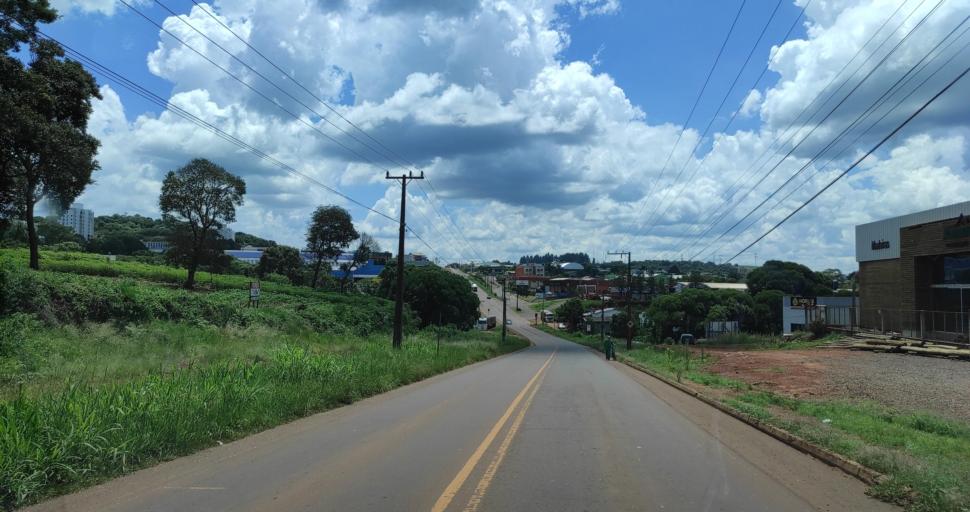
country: BR
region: Santa Catarina
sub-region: Xanxere
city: Xanxere
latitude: -26.8627
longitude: -52.4073
